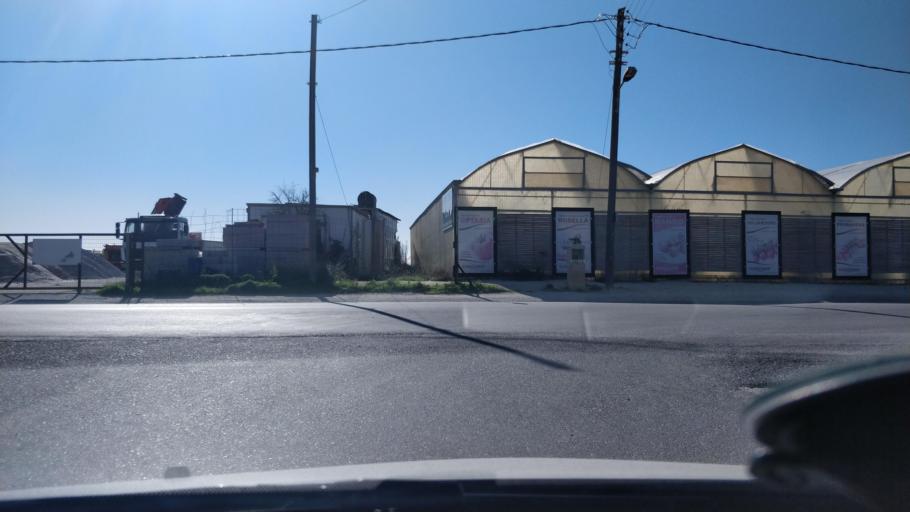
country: GR
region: Crete
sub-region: Nomos Lasithiou
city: Gra Liyia
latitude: 35.0137
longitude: 25.6770
